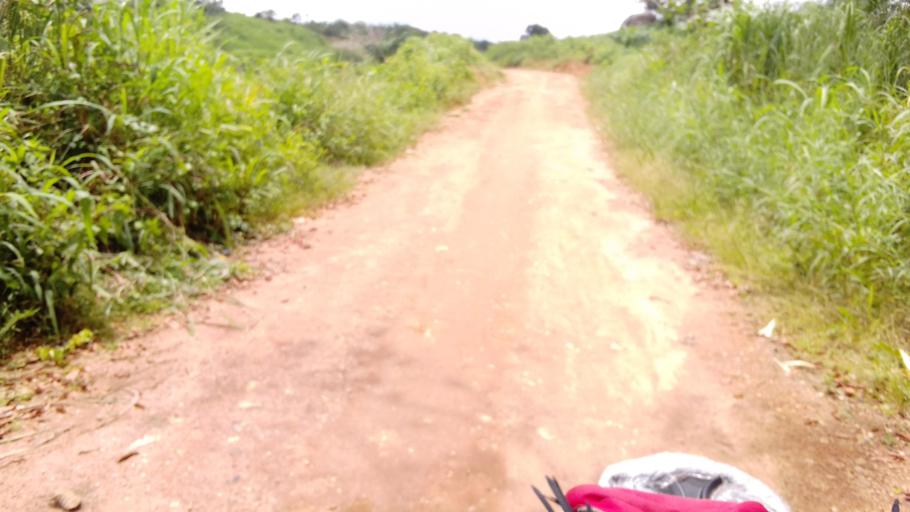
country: SL
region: Eastern Province
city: Koidu
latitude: 8.6651
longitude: -10.9428
